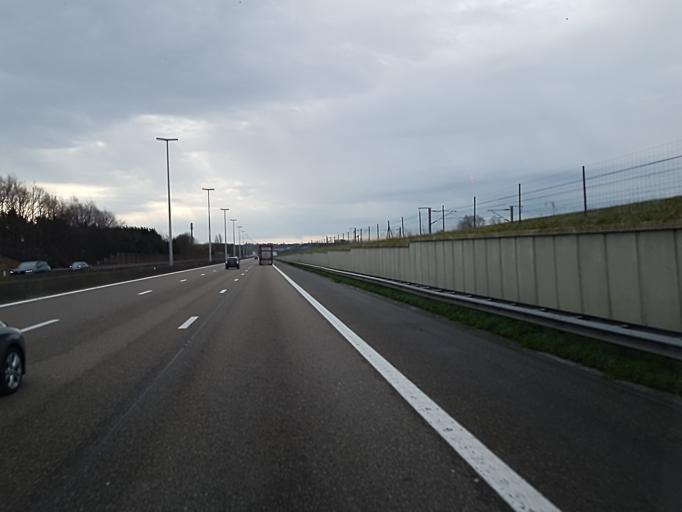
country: BE
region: Flanders
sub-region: Provincie Vlaams-Brabant
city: Hoegaarden
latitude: 50.7906
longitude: 4.9039
